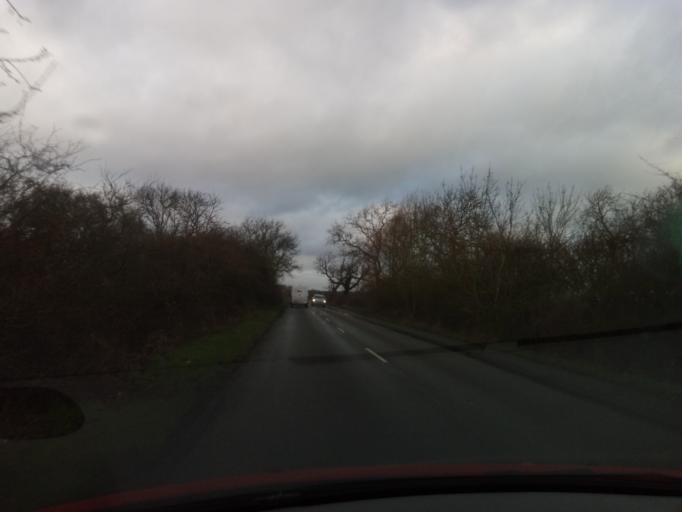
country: GB
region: England
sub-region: Leicestershire
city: Sileby
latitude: 52.7308
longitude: -1.1235
